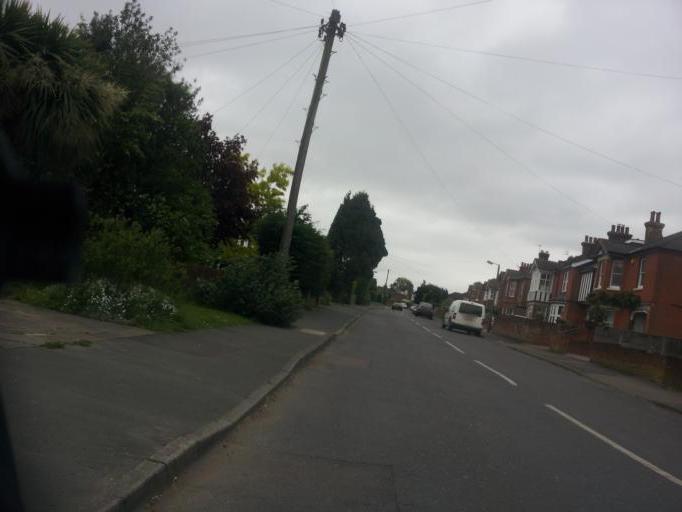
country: GB
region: England
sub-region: Kent
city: Maidstone
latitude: 51.2516
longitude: 0.5284
